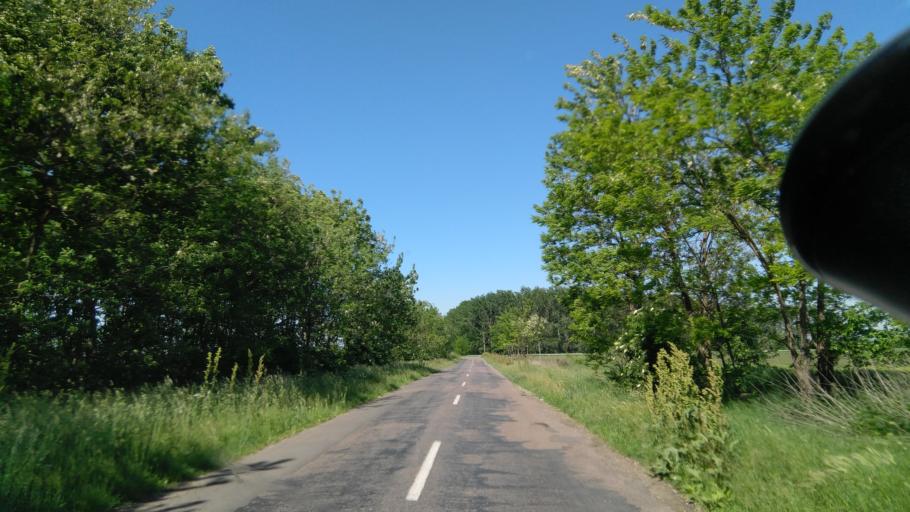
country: HU
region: Bekes
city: Kunagota
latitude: 46.4256
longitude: 21.0894
